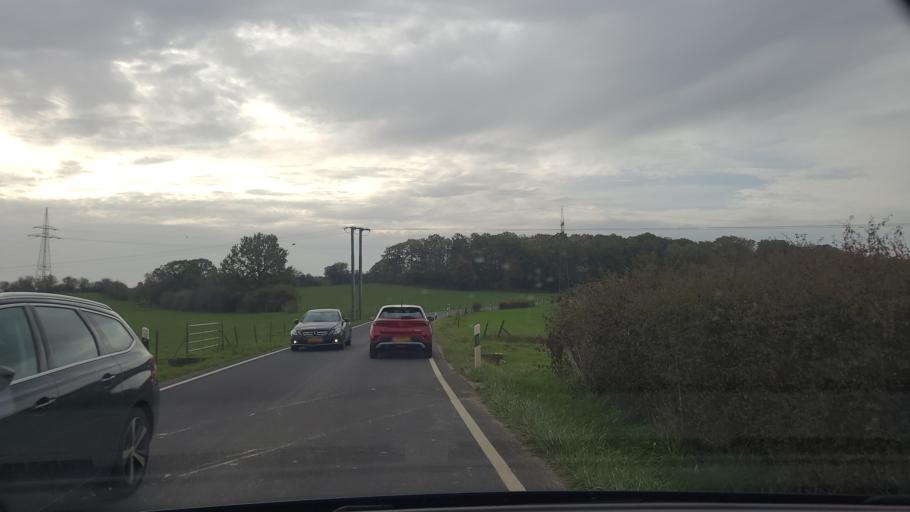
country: LU
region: Luxembourg
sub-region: Canton de Capellen
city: Mamer
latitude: 49.6202
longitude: 6.0208
